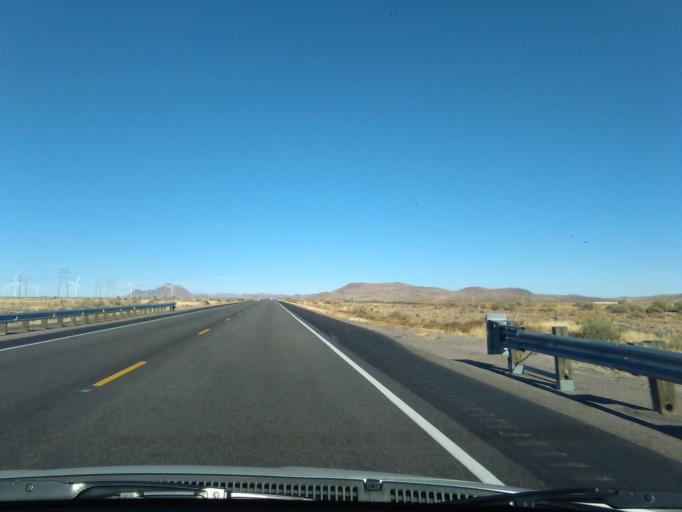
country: US
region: New Mexico
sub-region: Luna County
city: Deming
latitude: 32.4976
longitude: -107.5149
